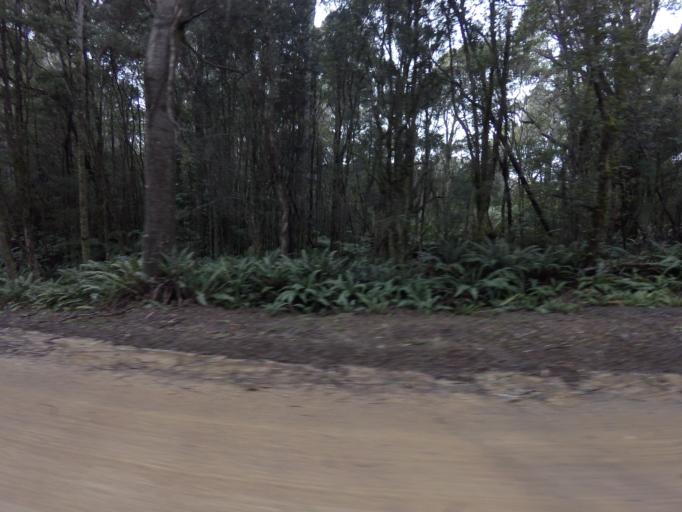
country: AU
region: Tasmania
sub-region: Huon Valley
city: Geeveston
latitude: -43.5532
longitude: 146.8842
